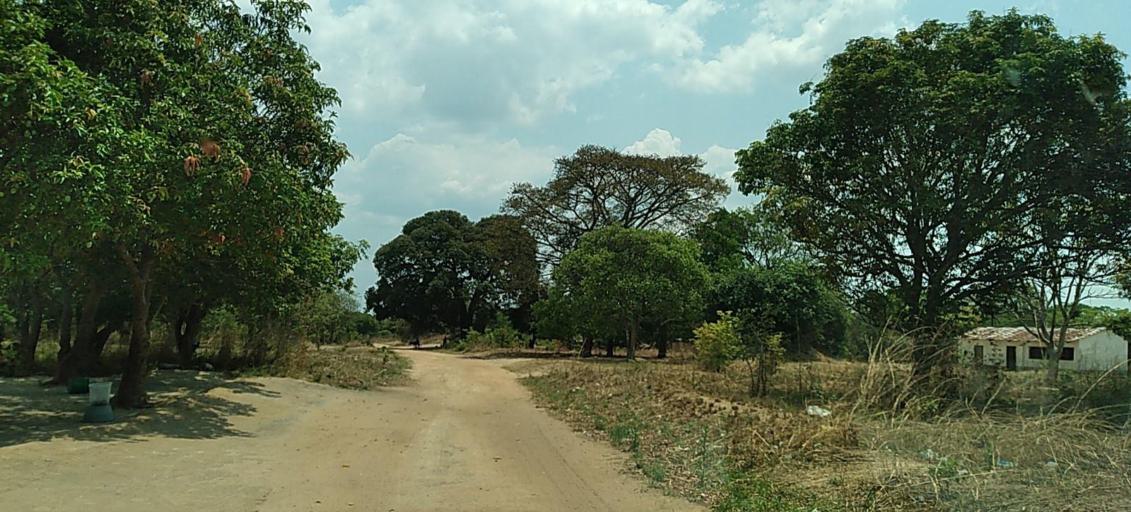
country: ZM
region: Copperbelt
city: Luanshya
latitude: -13.1593
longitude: 28.3091
